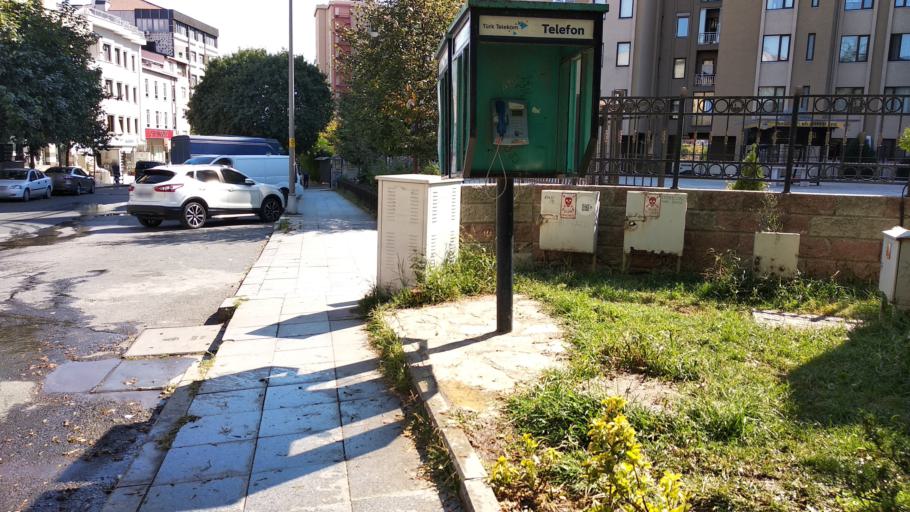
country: TR
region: Istanbul
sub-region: Atasehir
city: Atasehir
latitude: 41.0027
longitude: 29.0752
